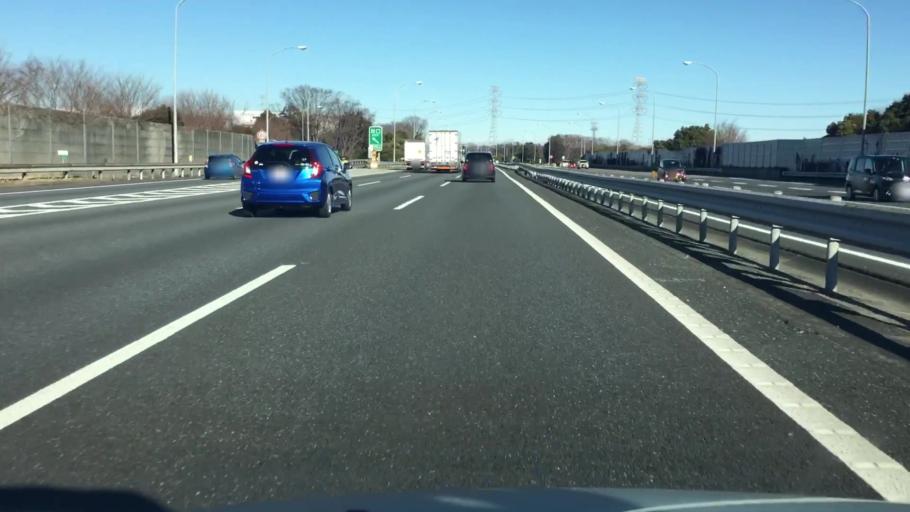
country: JP
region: Saitama
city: Sakado
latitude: 36.0237
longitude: 139.3820
